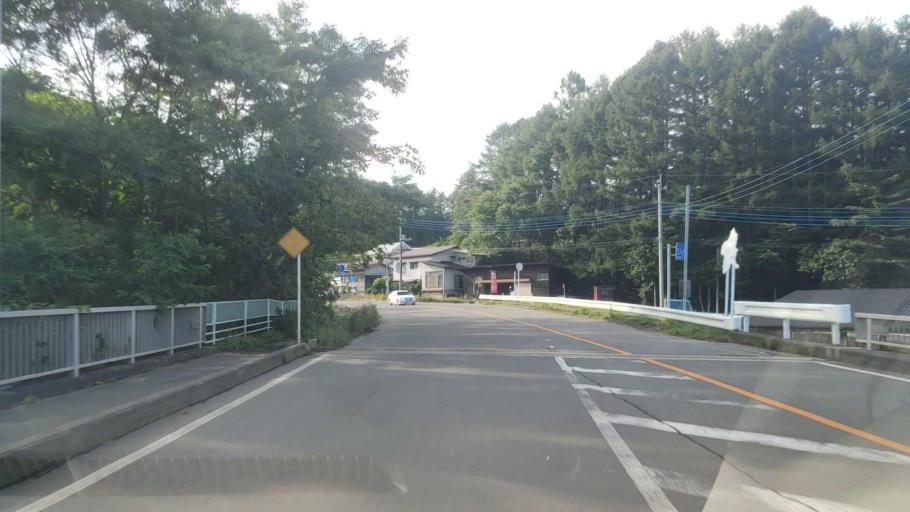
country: JP
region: Nagano
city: Komoro
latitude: 36.4872
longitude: 138.4451
